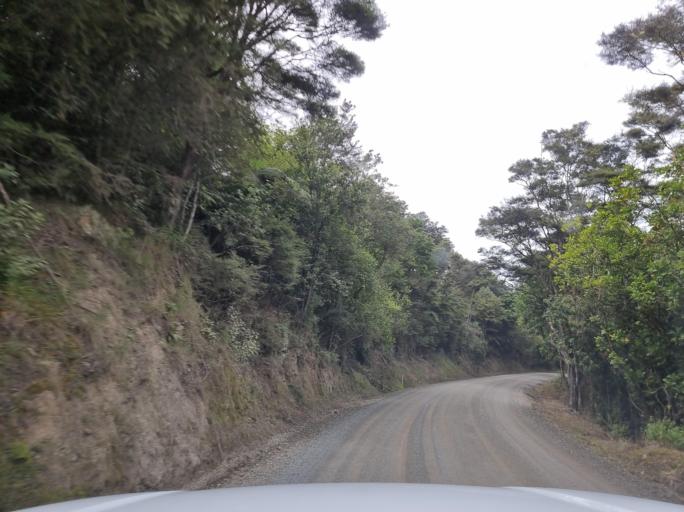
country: NZ
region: Northland
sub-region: Whangarei
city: Ruakaka
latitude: -36.0404
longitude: 174.4098
